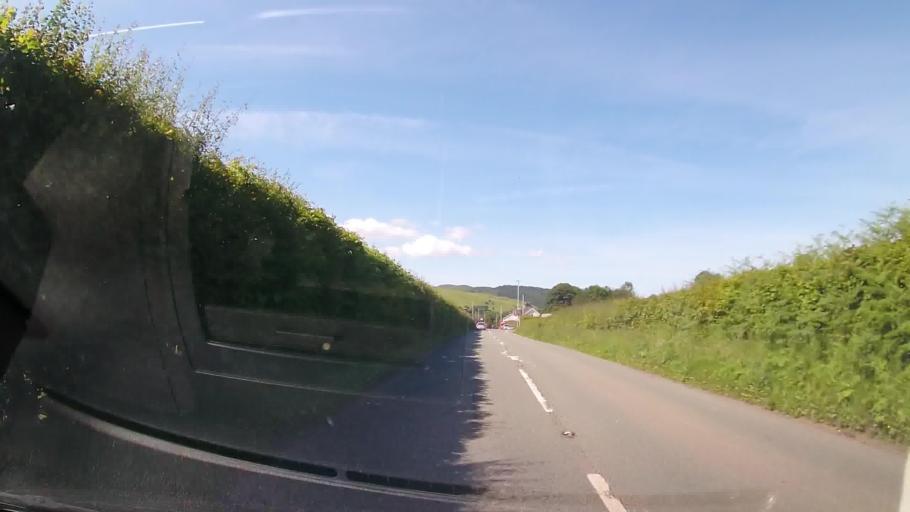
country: GB
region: Wales
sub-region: Sir Powys
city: Machynlleth
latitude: 52.5947
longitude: -3.8045
